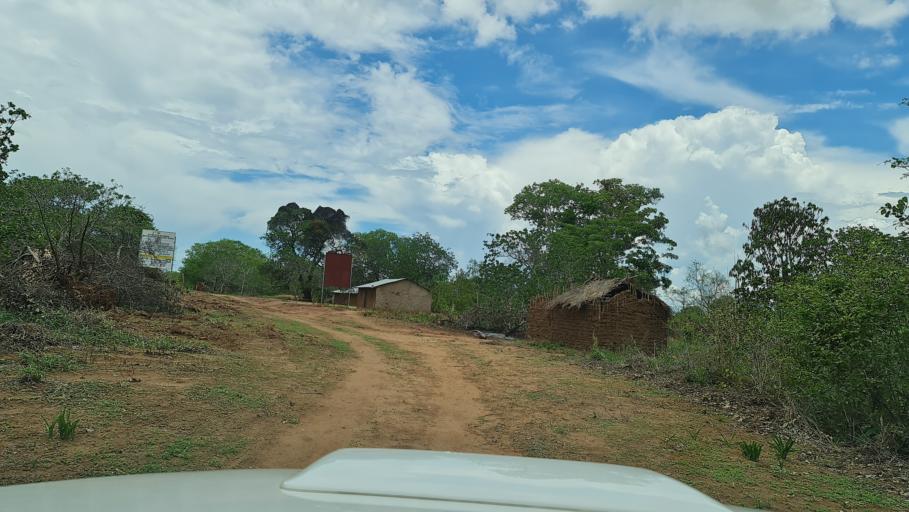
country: MZ
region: Nampula
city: Ilha de Mocambique
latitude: -15.5139
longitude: 40.2024
